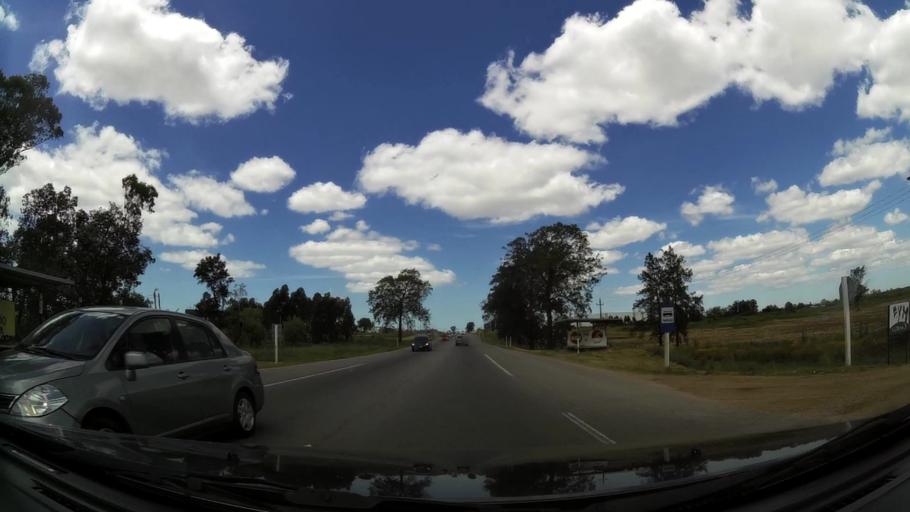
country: UY
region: Canelones
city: Colonia Nicolich
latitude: -34.8078
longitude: -56.0059
